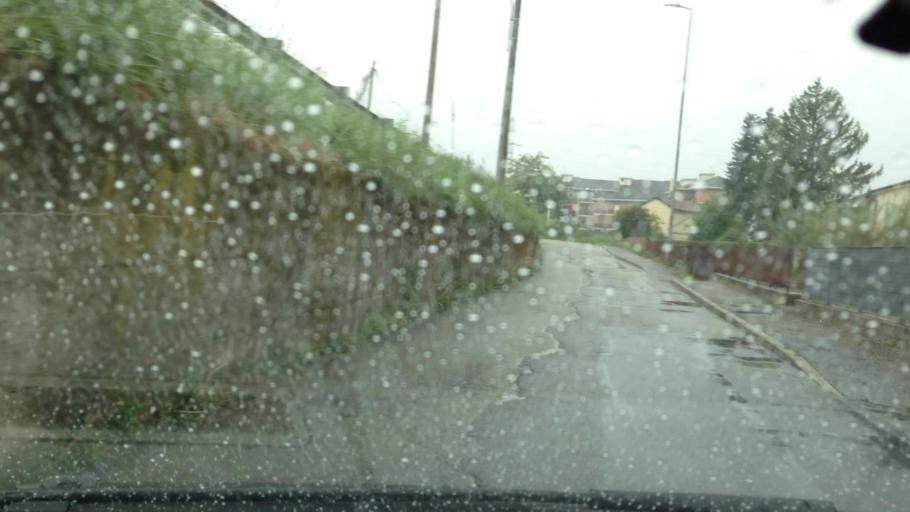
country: IT
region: Piedmont
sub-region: Provincia di Asti
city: Asti
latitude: 44.8999
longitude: 8.2295
